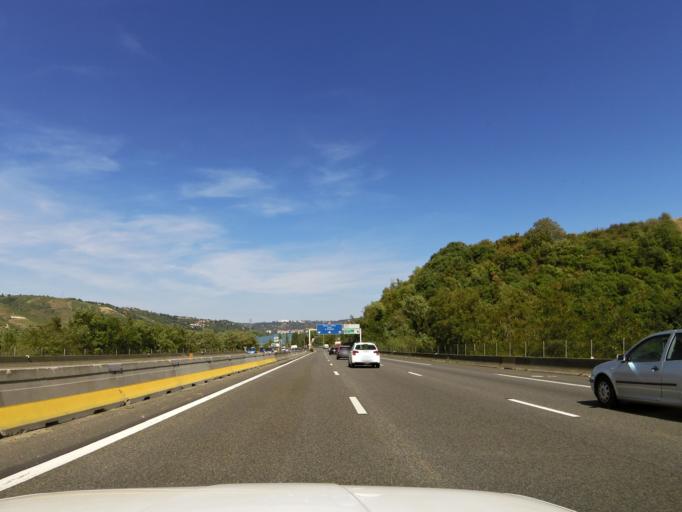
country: FR
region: Rhone-Alpes
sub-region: Departement du Rhone
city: Saint-Cyr-sur-le-Rhone
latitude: 45.4940
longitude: 4.8356
